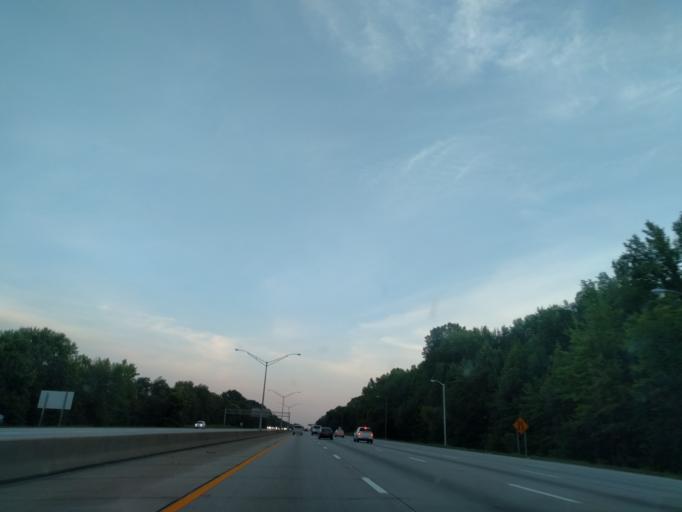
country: US
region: Kentucky
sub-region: Jefferson County
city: Heritage Creek
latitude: 38.1084
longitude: -85.7015
